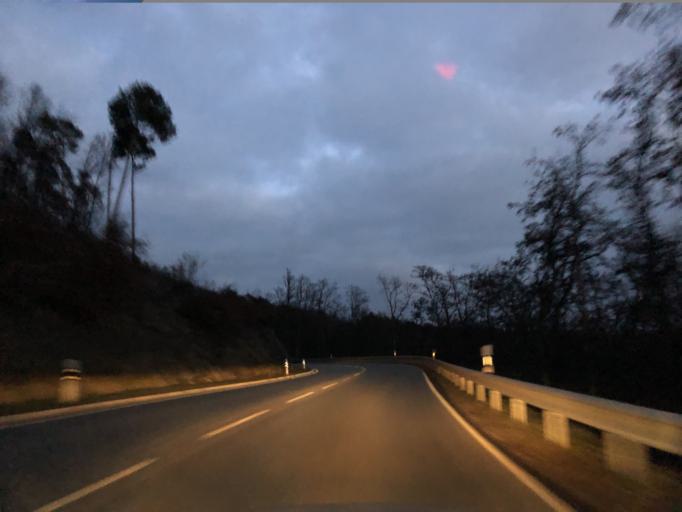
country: DE
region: Rheinland-Pfalz
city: Nassau
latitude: 50.2978
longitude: 7.8126
